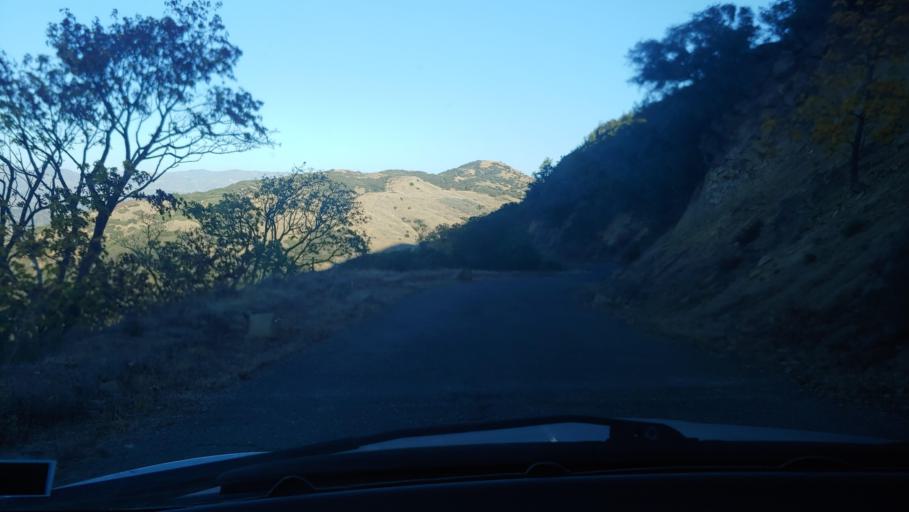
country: US
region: California
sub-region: Santa Barbara County
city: Mission Canyon
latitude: 34.5067
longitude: -119.7593
